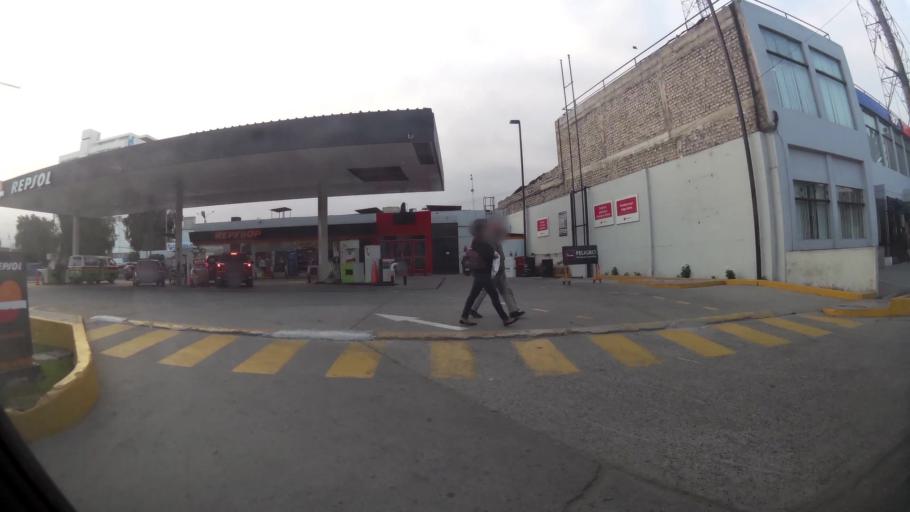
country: PE
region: La Libertad
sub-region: Provincia de Trujillo
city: Trujillo
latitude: -8.1012
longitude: -79.0357
